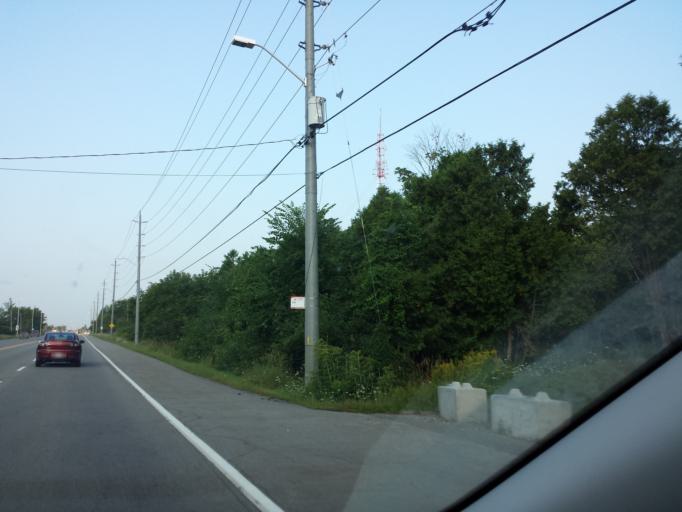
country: CA
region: Ontario
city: Bells Corners
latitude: 45.3076
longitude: -75.8683
